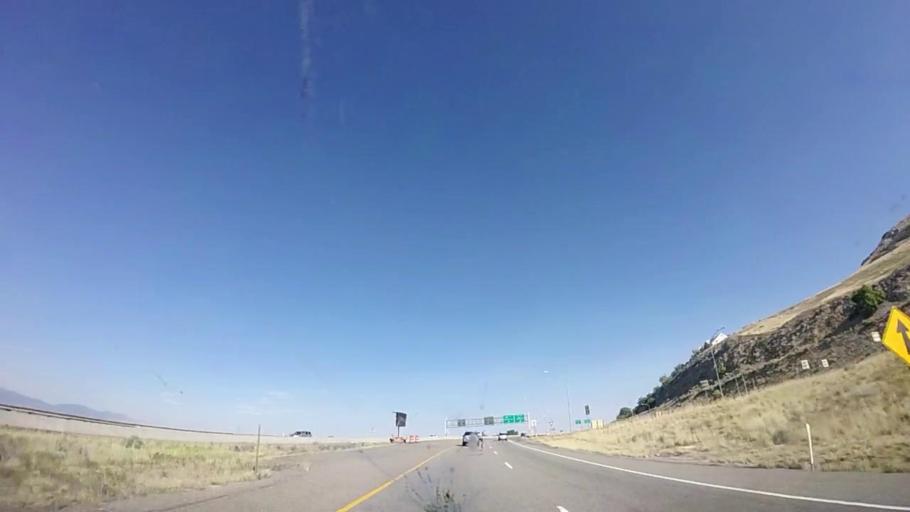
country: US
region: Utah
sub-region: Salt Lake County
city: East Millcreek
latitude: 40.7123
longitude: -111.8043
